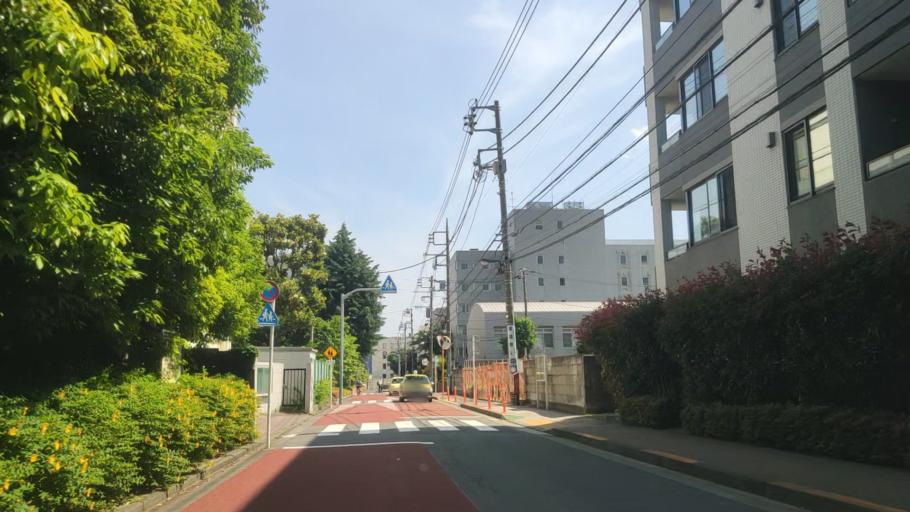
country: JP
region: Tokyo
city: Tokyo
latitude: 35.6549
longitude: 139.6840
